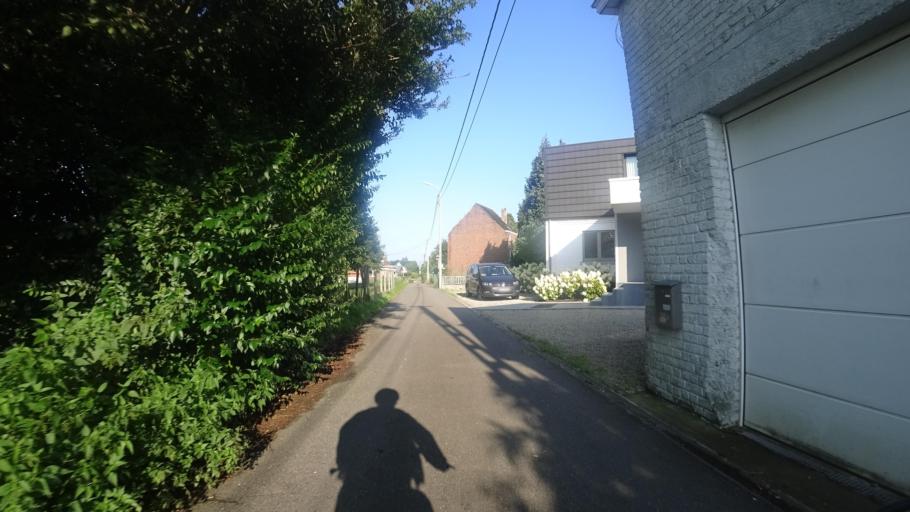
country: BE
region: Flanders
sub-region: Provincie Vlaams-Brabant
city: Overijse
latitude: 50.7803
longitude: 4.5238
